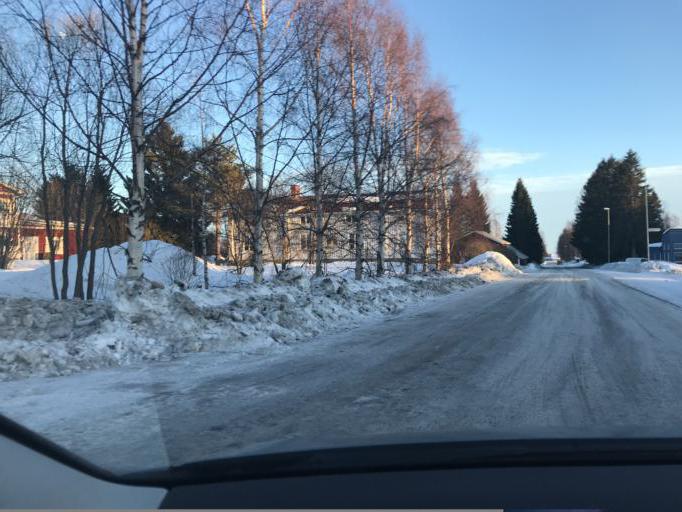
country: SE
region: Norrbotten
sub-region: Lulea Kommun
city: Sodra Sunderbyn
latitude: 65.6607
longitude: 21.9435
